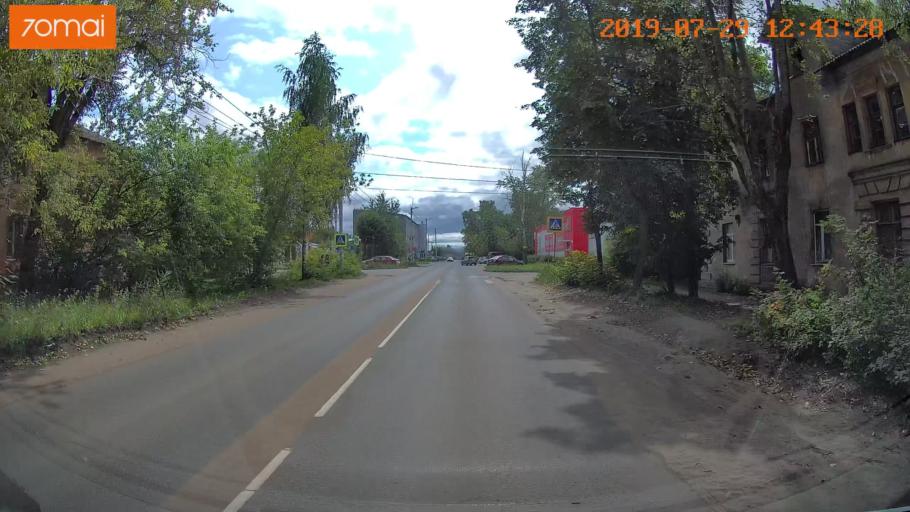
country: RU
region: Ivanovo
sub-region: Gorod Ivanovo
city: Ivanovo
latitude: 57.0023
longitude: 40.9306
